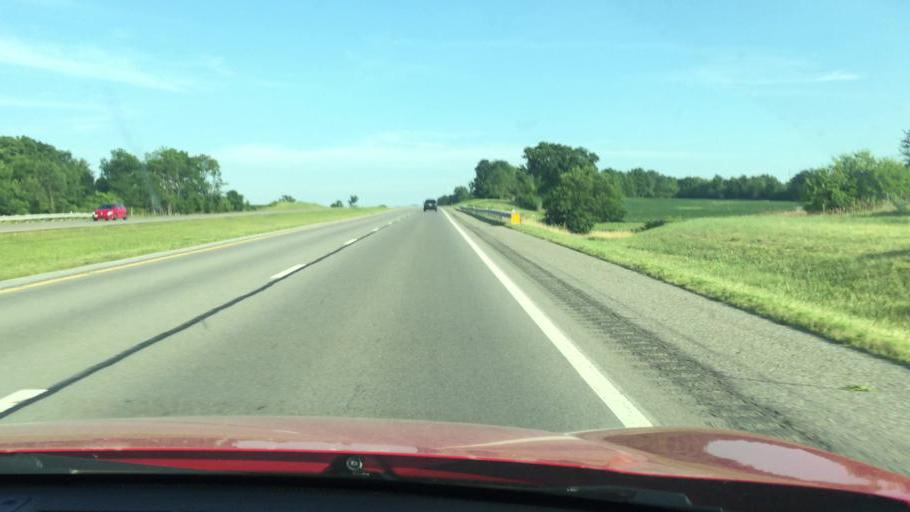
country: US
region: Ohio
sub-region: Logan County
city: Bellefontaine
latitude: 40.3973
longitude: -83.7814
